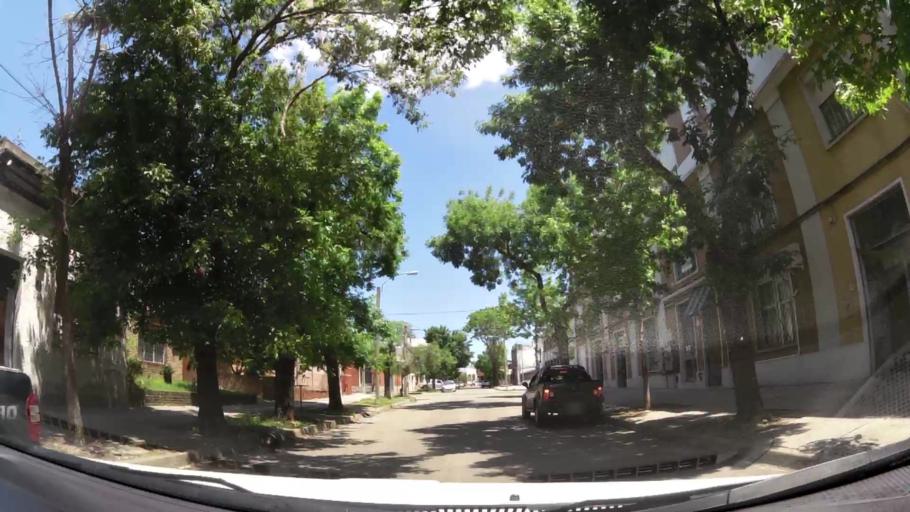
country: UY
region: Montevideo
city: Montevideo
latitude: -34.8684
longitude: -56.1900
